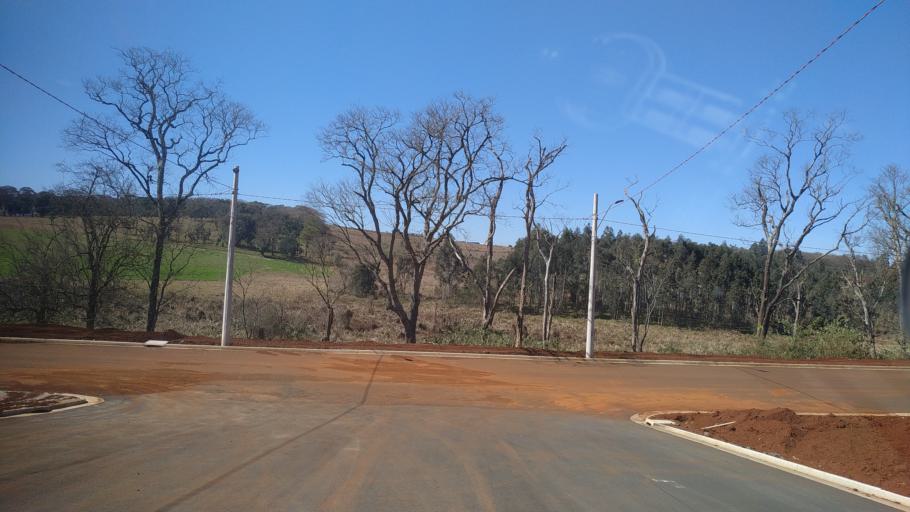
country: BR
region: Santa Catarina
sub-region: Chapeco
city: Chapeco
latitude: -27.0900
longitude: -52.7059
